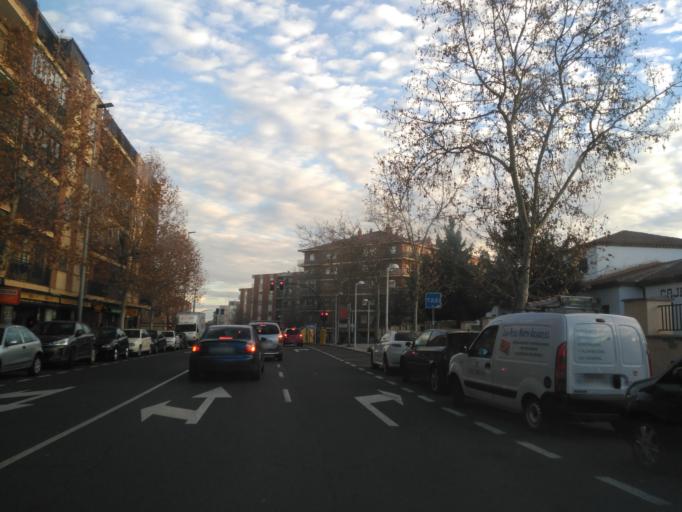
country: ES
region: Castille and Leon
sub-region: Provincia de Salamanca
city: Salamanca
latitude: 40.9753
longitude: -5.6736
